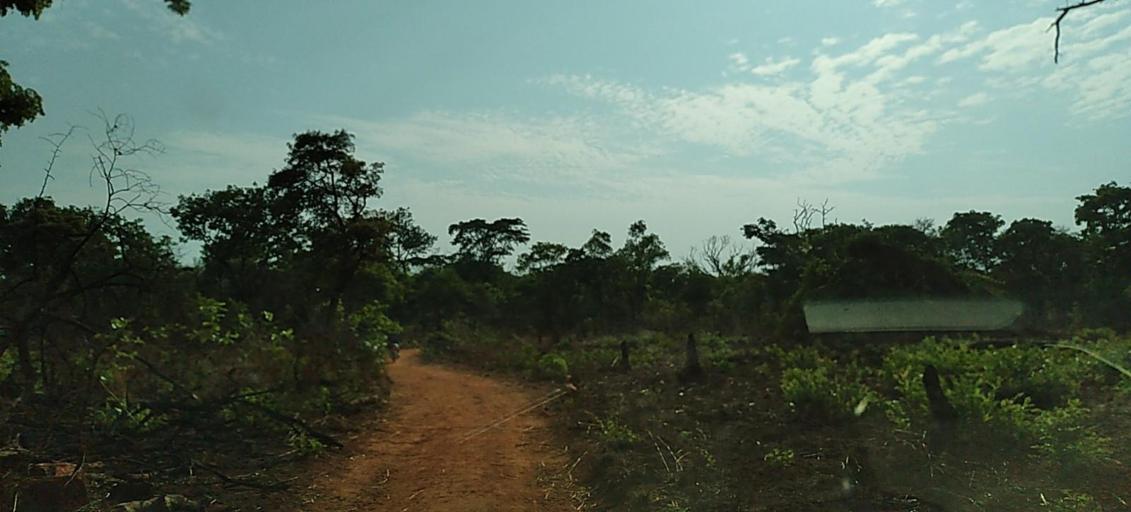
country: ZM
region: Copperbelt
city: Kalulushi
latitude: -12.9632
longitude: 27.7077
